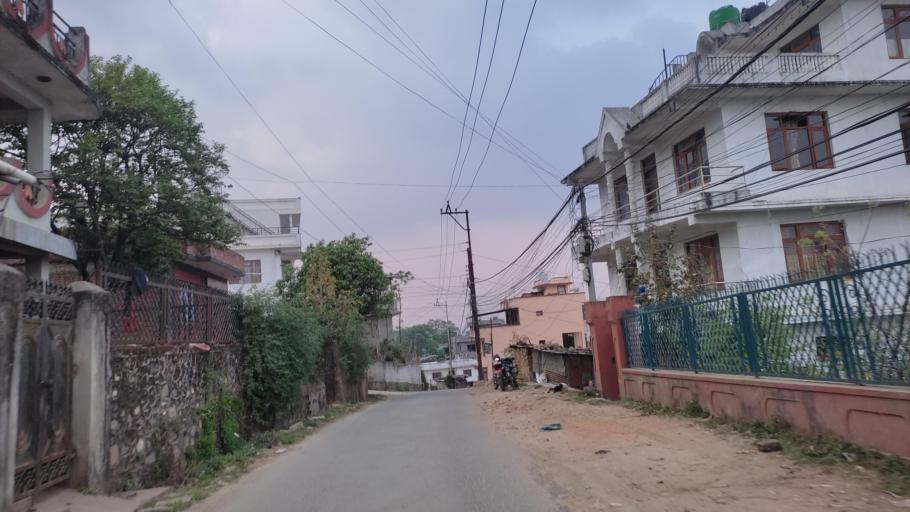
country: NP
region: Central Region
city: Kirtipur
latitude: 27.6724
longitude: 85.2414
